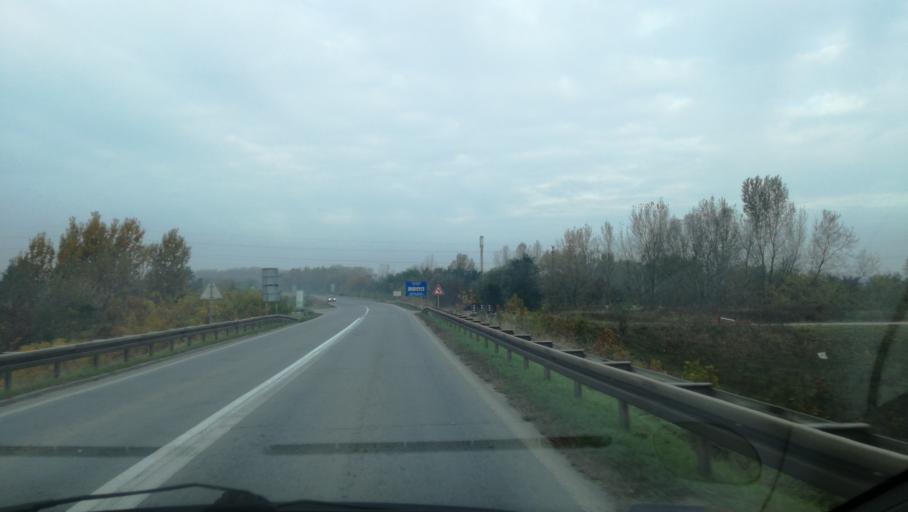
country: RS
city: Taras
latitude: 45.3989
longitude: 20.2093
